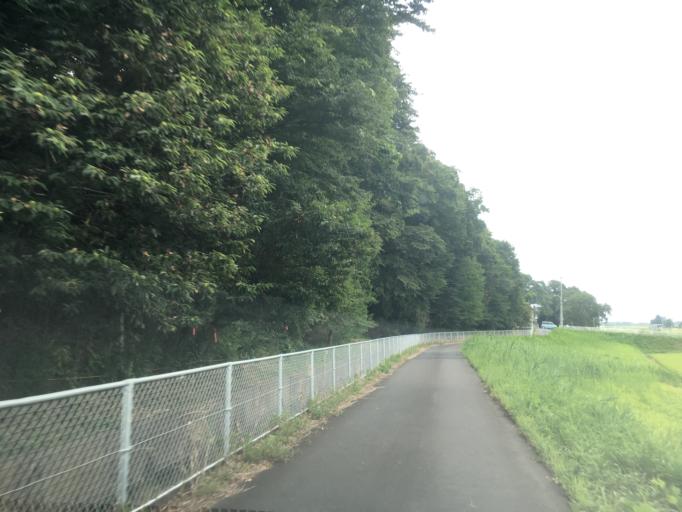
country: JP
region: Ibaraki
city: Katsuta
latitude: 36.3782
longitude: 140.5220
